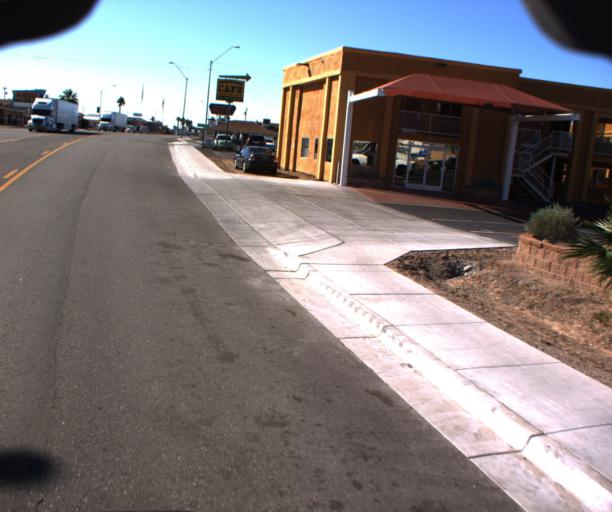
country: US
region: Arizona
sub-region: La Paz County
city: Parker
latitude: 34.1539
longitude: -114.2916
